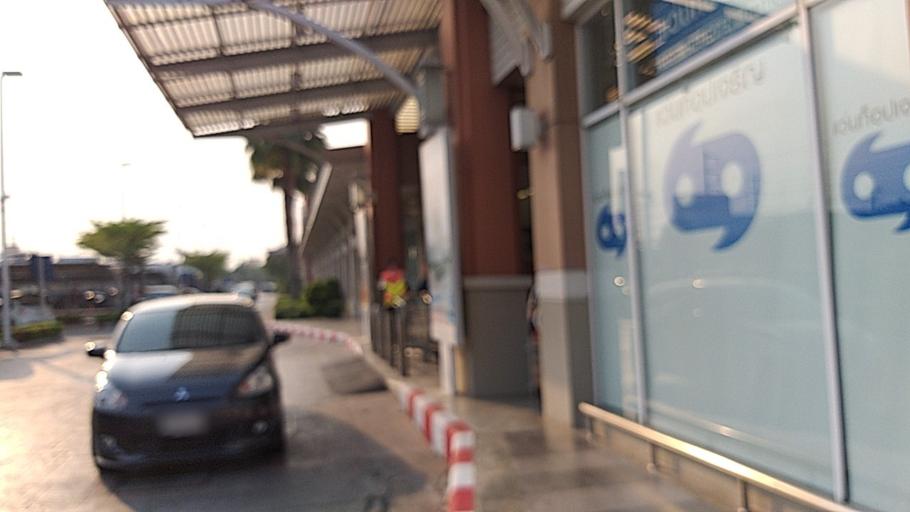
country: TH
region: Pathum Thani
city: Lam Luk Ka
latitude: 13.9347
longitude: 100.7191
